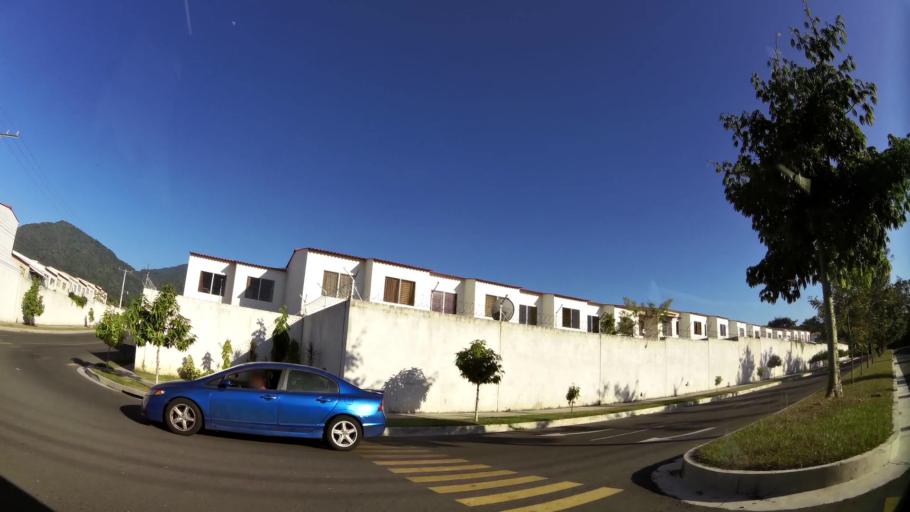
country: SV
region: La Libertad
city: Santa Tecla
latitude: 13.7397
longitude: -89.3502
